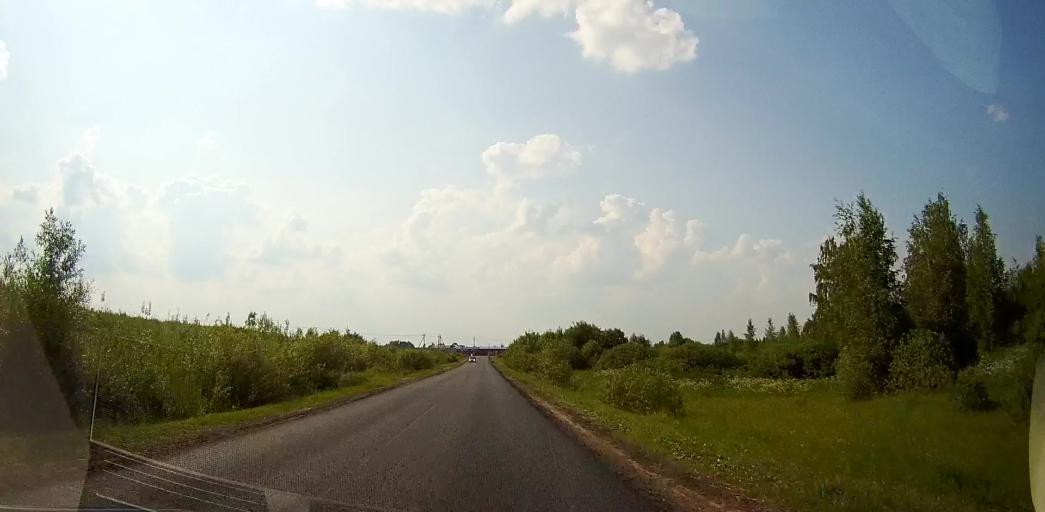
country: RU
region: Moskovskaya
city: Il'inskoye
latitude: 55.2214
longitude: 37.9312
